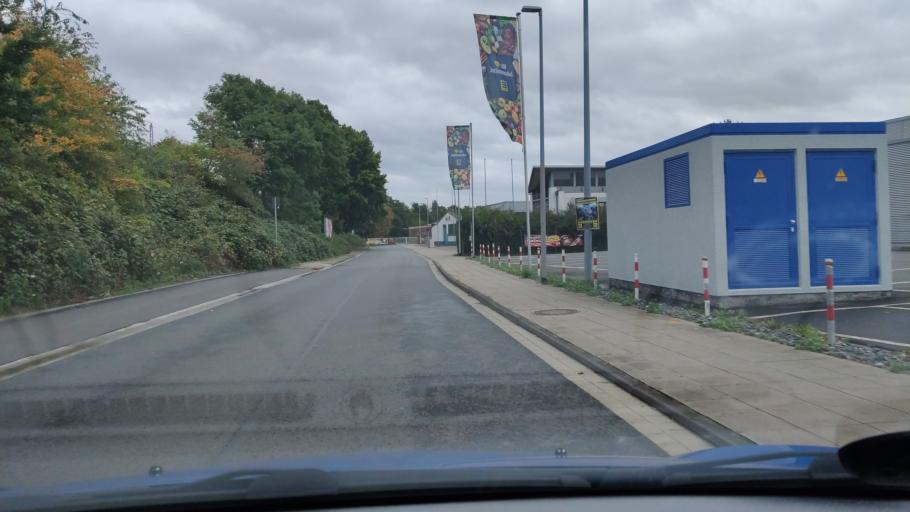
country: DE
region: Lower Saxony
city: Hannover
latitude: 52.3855
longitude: 9.6706
